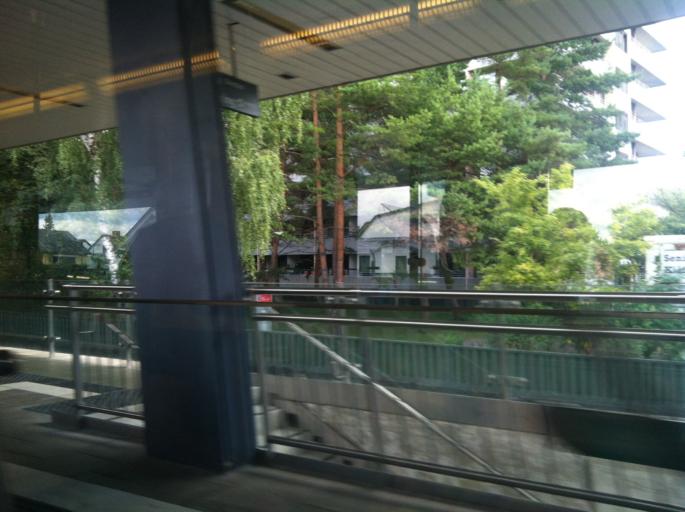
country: DE
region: Bavaria
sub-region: Upper Bavaria
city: Unterfoehring
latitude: 48.2030
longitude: 11.6131
